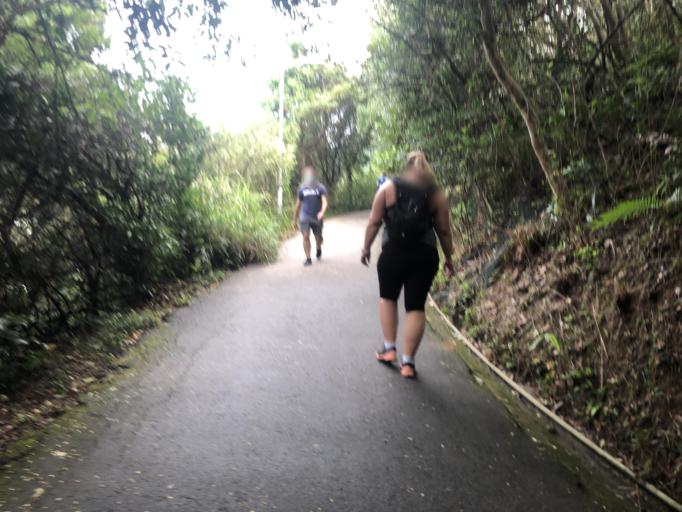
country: HK
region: Central and Western
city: Central
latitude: 22.2767
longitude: 114.1369
